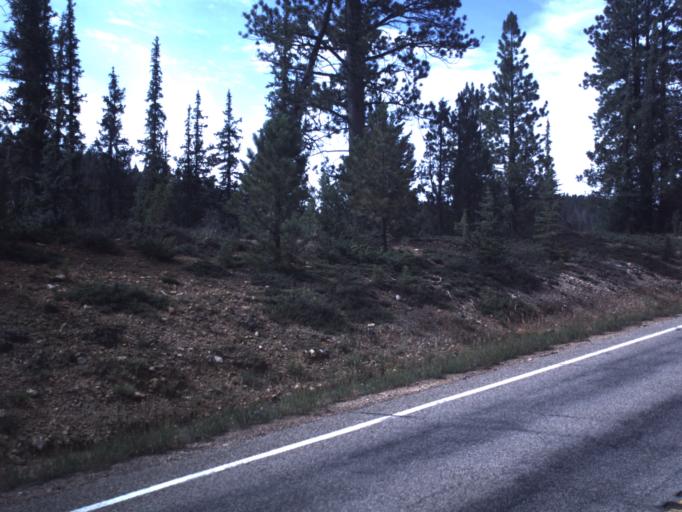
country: US
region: Utah
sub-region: Garfield County
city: Panguitch
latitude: 37.4972
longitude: -112.6041
